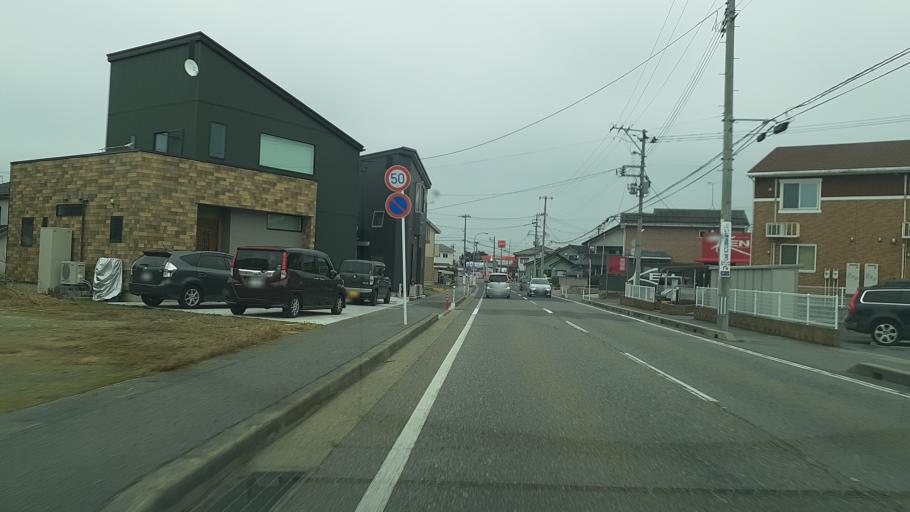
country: JP
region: Niigata
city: Niigata-shi
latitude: 37.8546
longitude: 139.0362
